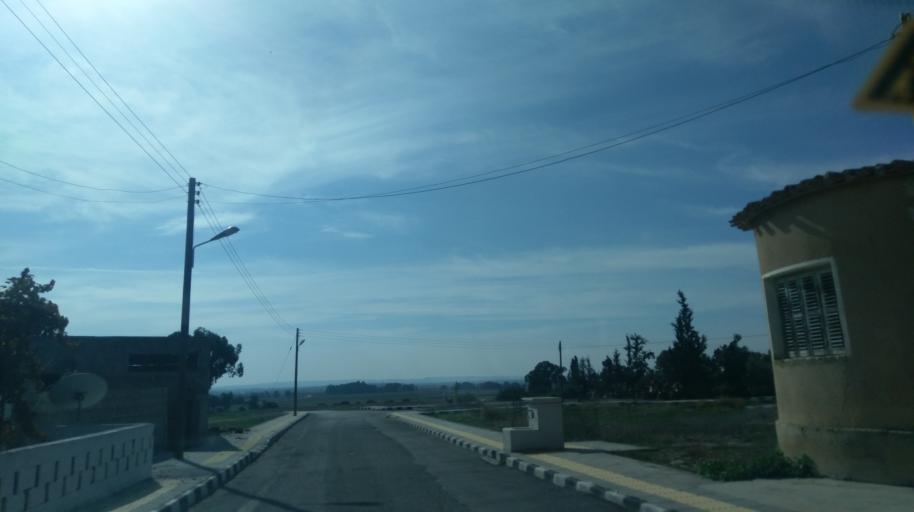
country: CY
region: Ammochostos
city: Lefkonoiko
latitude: 35.2163
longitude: 33.6985
